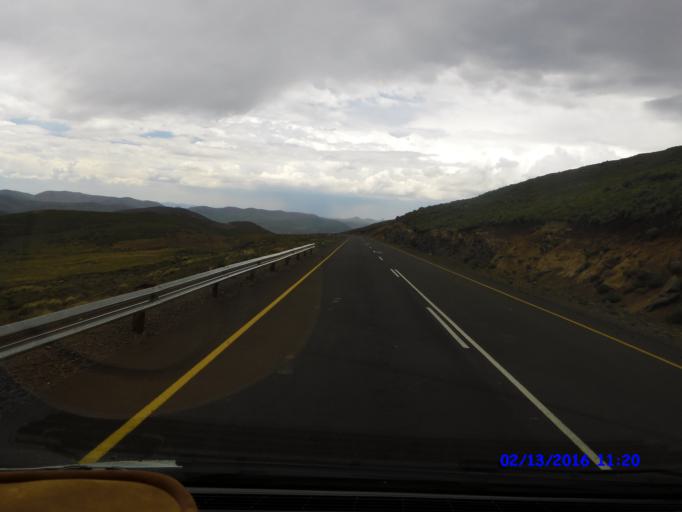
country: LS
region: Maseru
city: Nako
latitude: -29.7534
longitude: 27.9631
